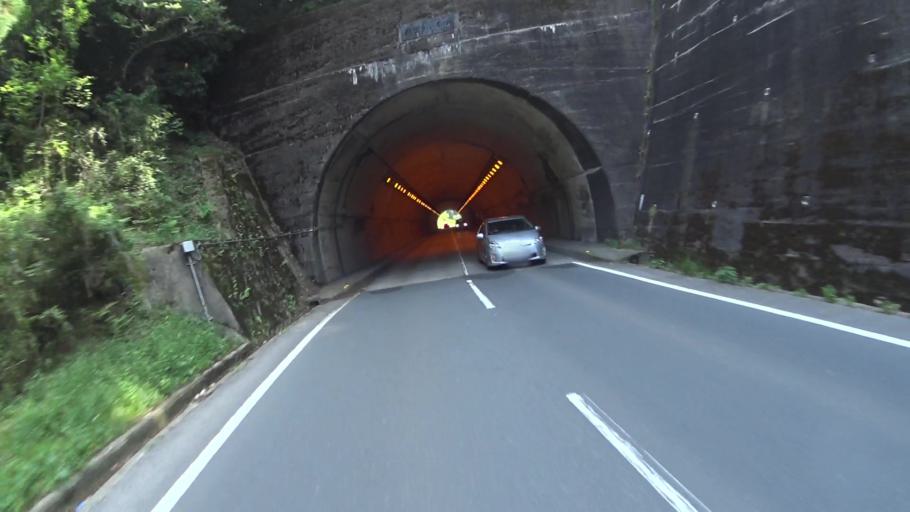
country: JP
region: Kyoto
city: Kameoka
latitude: 35.1388
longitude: 135.4920
